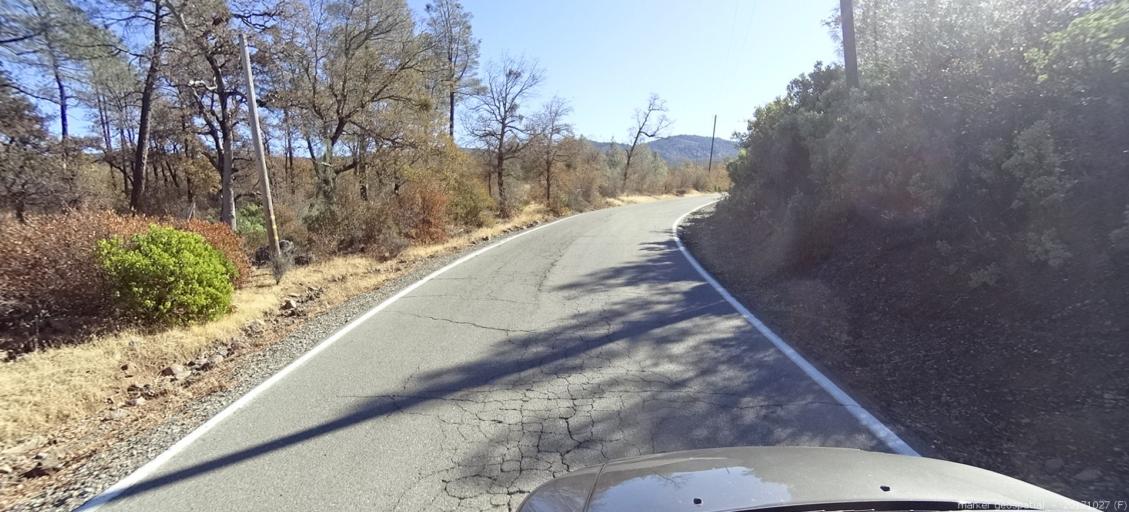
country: US
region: California
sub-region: Shasta County
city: Burney
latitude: 40.7982
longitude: -121.9256
